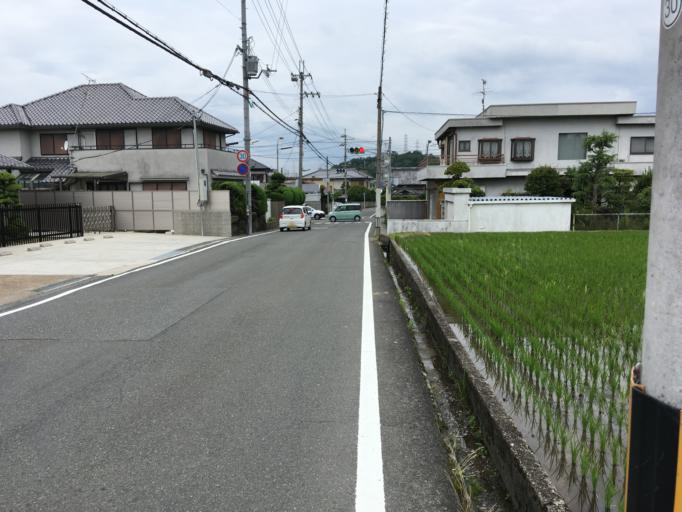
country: JP
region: Nara
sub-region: Ikoma-shi
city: Ikoma
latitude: 34.7224
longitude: 135.7045
